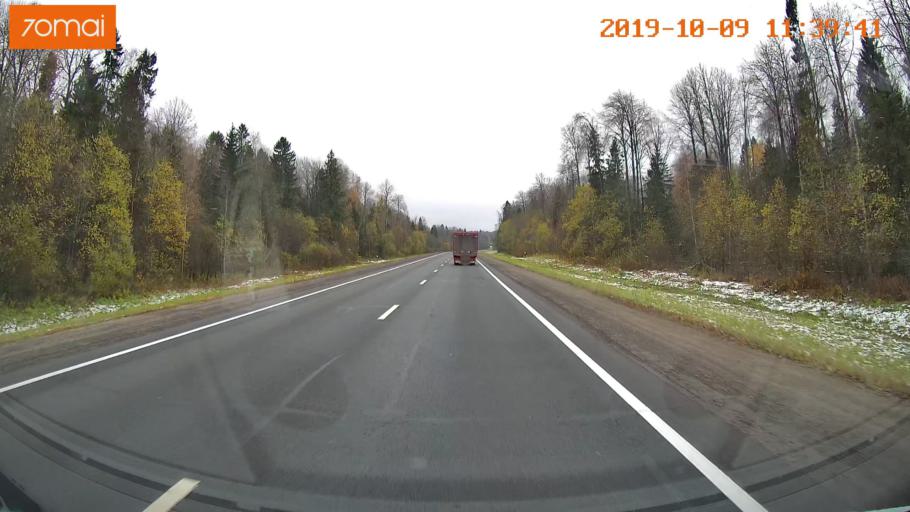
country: RU
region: Vologda
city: Gryazovets
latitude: 58.9530
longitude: 40.1685
